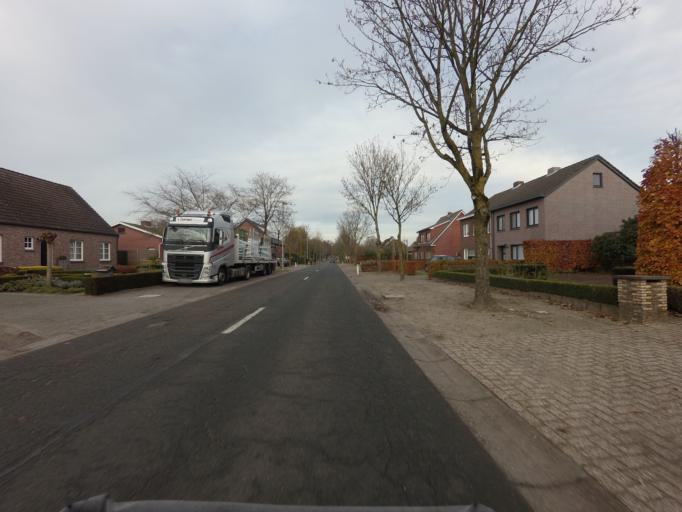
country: BE
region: Flanders
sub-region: Provincie Antwerpen
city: Hoogstraten
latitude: 51.4772
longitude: 4.8081
